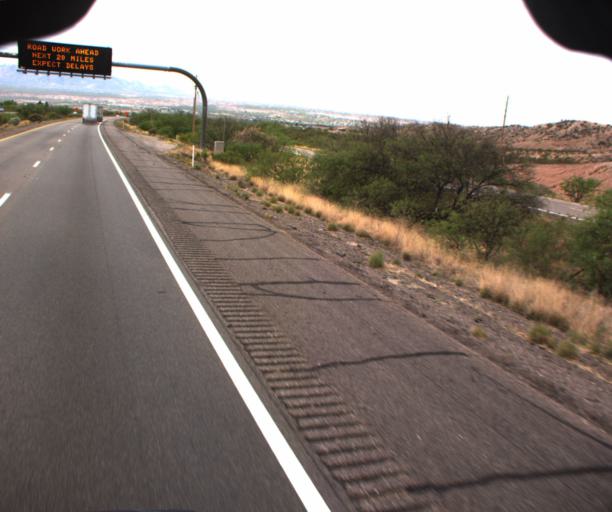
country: US
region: Arizona
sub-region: Cochise County
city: Benson
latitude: 31.9719
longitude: -110.2385
